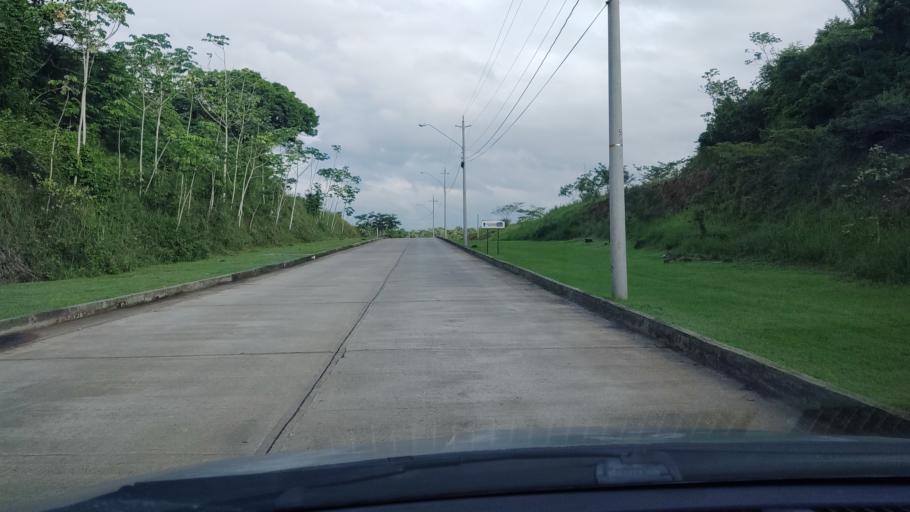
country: PA
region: Panama
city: Nuevo Arraijan
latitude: 8.9253
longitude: -79.7552
